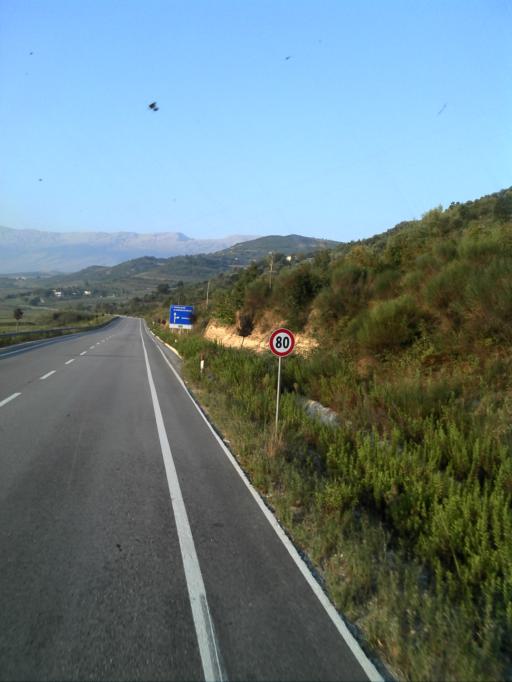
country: AL
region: Gjirokaster
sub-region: Rrethi i Tepelenes
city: Krahes
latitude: 40.4624
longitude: 19.8518
